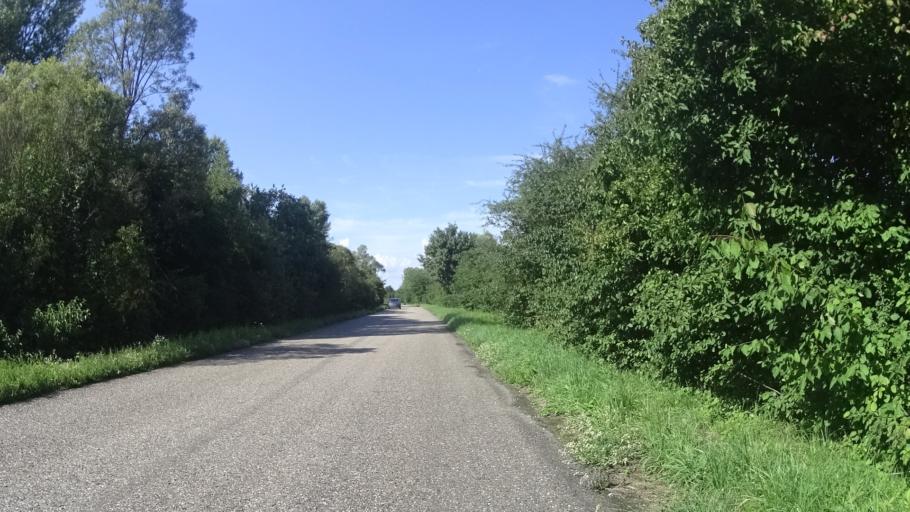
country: DE
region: Baden-Wuerttemberg
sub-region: Karlsruhe Region
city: Hugelsheim
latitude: 48.8249
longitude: 8.1016
